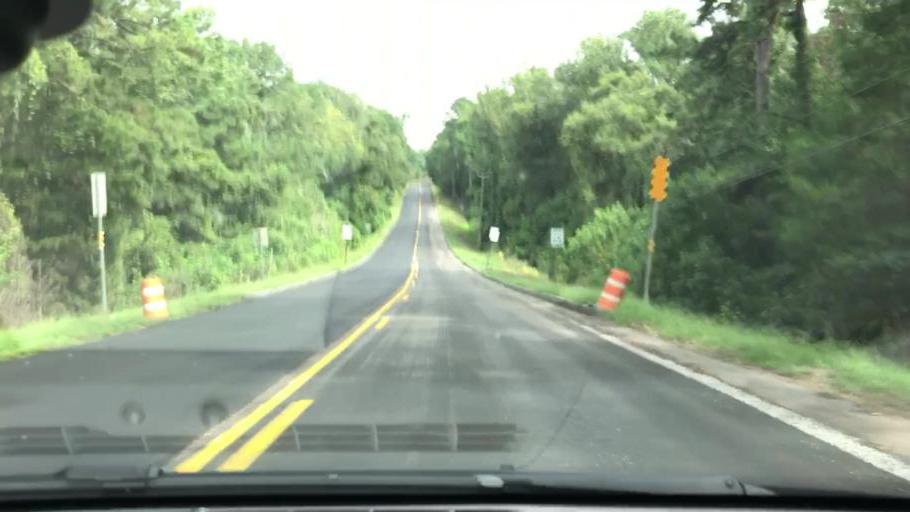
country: US
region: Georgia
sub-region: Clay County
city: Fort Gaines
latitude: 31.5962
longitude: -85.0439
